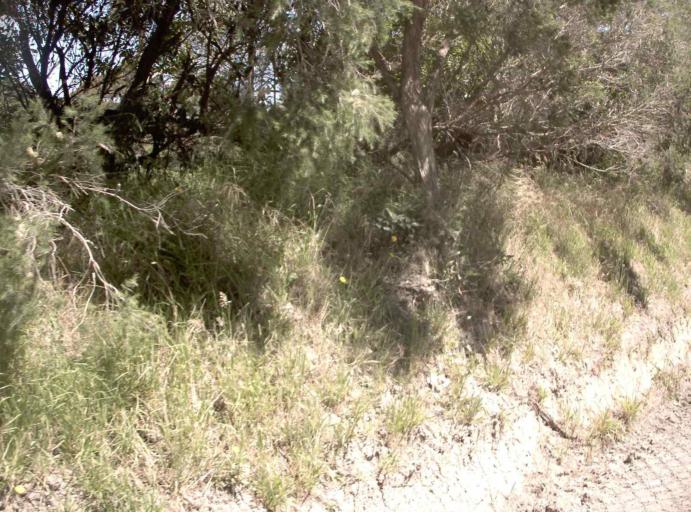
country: AU
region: Victoria
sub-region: Bass Coast
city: North Wonthaggi
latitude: -38.7643
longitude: 146.0647
